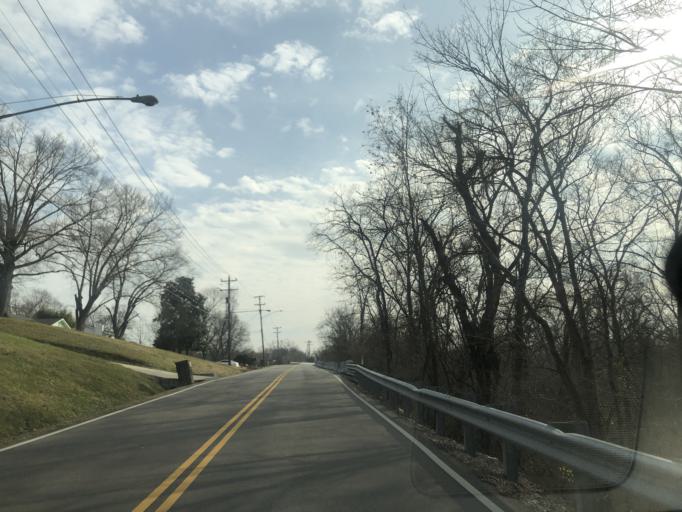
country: US
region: Tennessee
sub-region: Davidson County
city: Oak Hill
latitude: 36.1141
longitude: -86.7108
